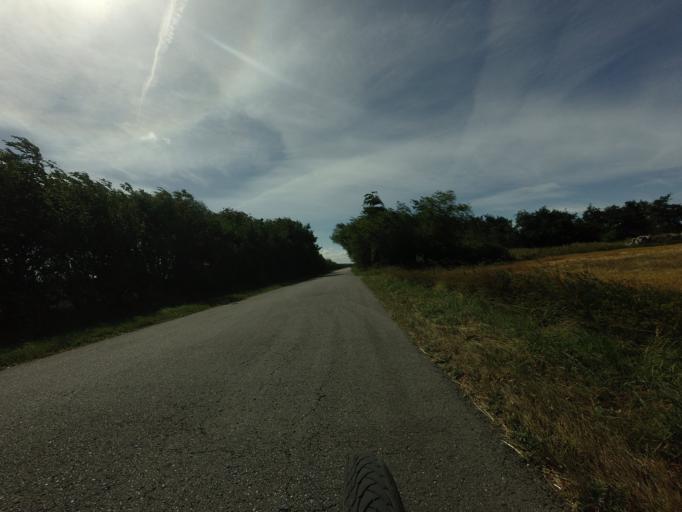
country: DK
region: North Denmark
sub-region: Bronderslev Kommune
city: Bronderslev
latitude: 57.3199
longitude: 9.8152
